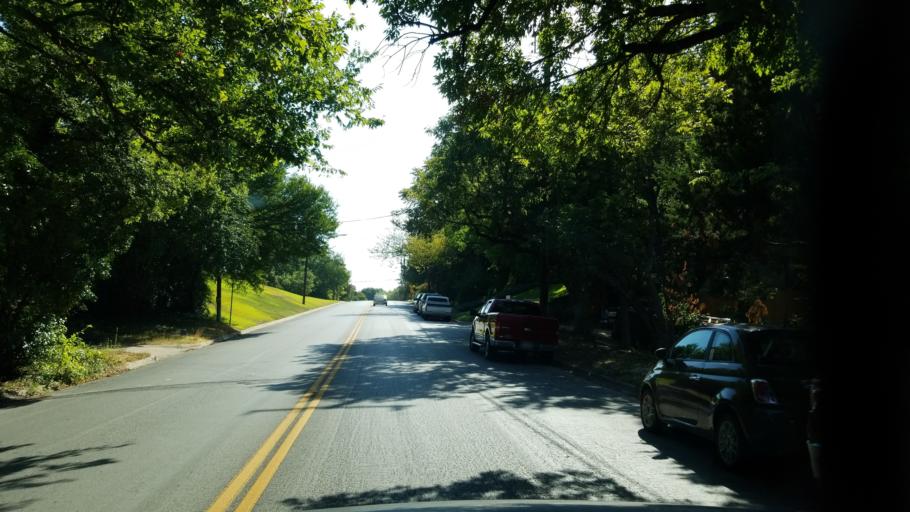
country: US
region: Texas
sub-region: Dallas County
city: Dallas
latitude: 32.7586
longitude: -96.8337
